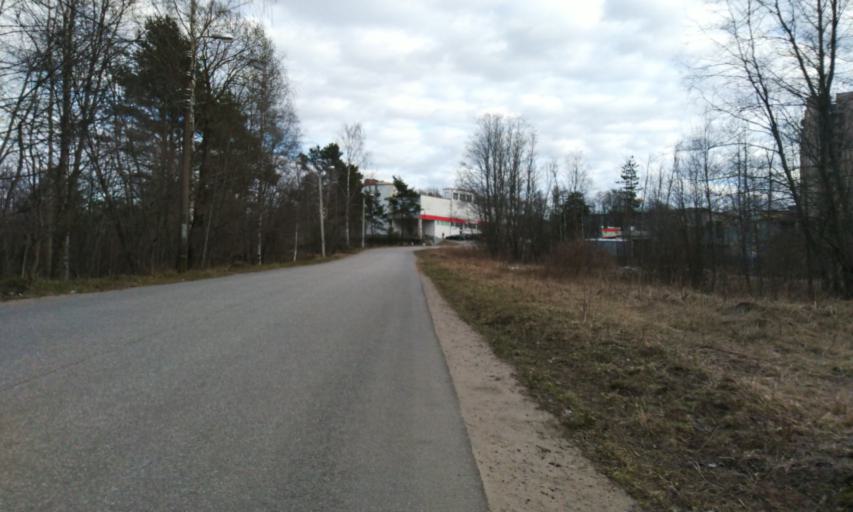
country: RU
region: Leningrad
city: Toksovo
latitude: 60.1140
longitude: 30.4893
